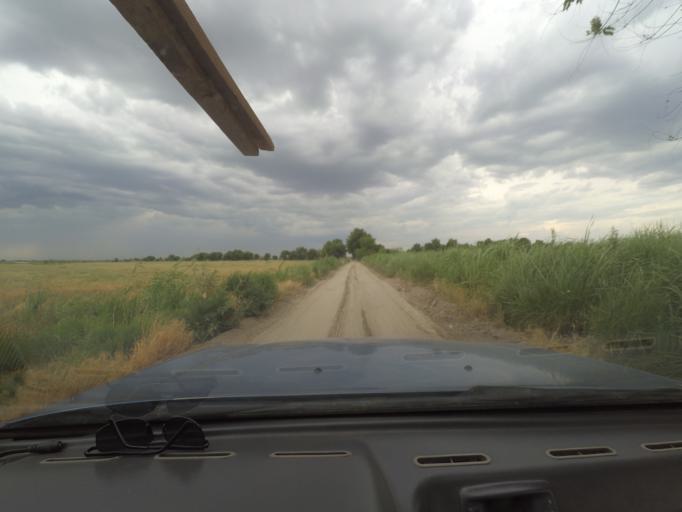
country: TJ
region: Viloyati Sughd
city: Buston
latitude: 40.5516
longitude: 69.0761
